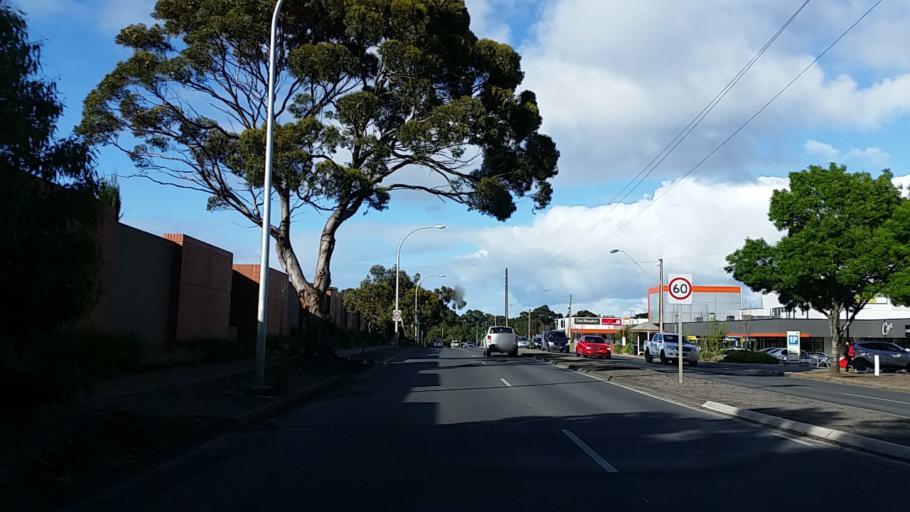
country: AU
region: South Australia
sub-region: Mitcham
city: Clapham
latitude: -35.0010
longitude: 138.5916
